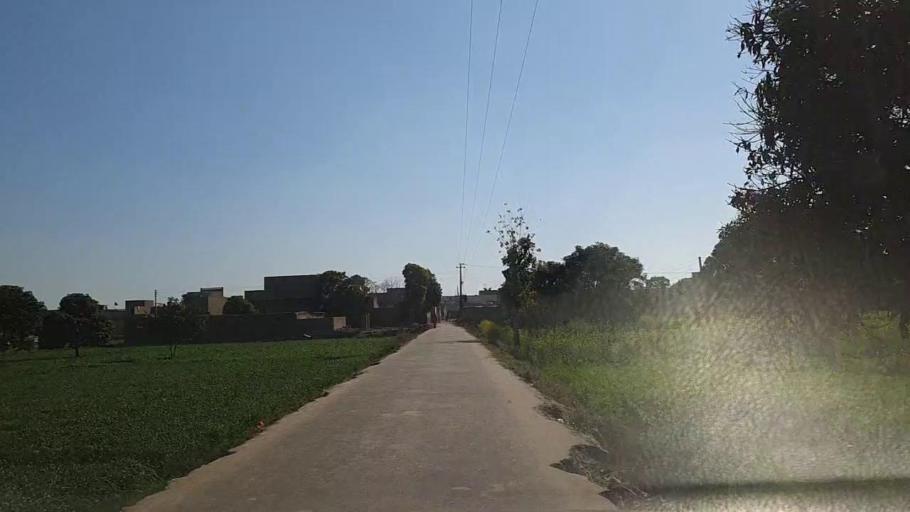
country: PK
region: Sindh
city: Nawabshah
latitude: 26.2572
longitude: 68.4242
